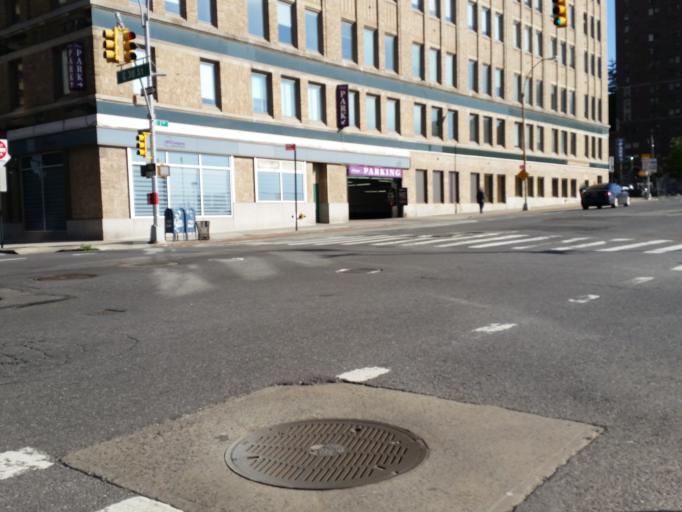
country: US
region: New York
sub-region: Queens County
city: Long Island City
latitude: 40.7461
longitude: -73.9716
